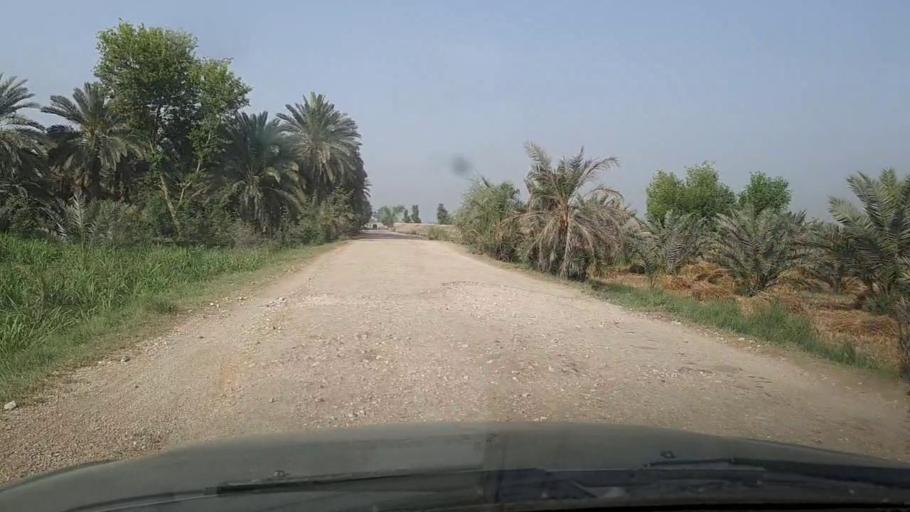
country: PK
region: Sindh
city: Pir jo Goth
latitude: 27.5365
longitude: 68.5141
